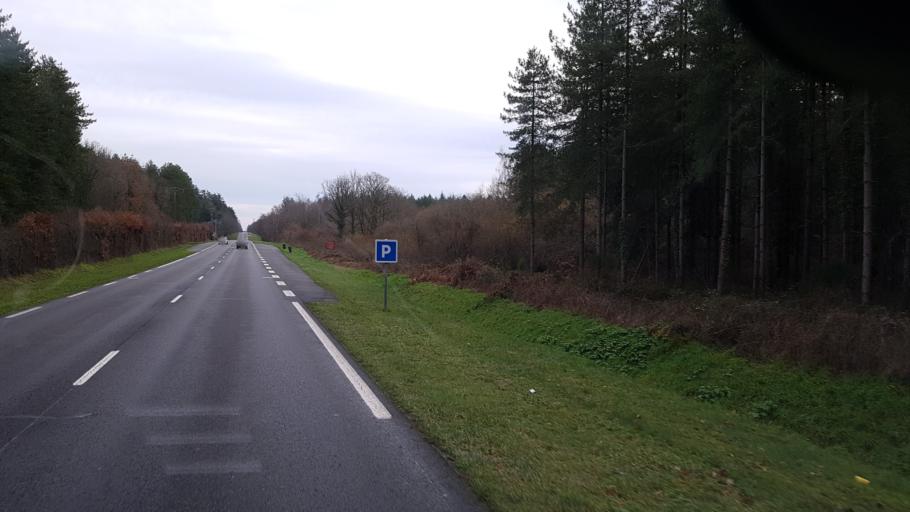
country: FR
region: Centre
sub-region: Departement du Loir-et-Cher
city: Lamotte-Beuvron
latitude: 47.6328
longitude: 2.0032
